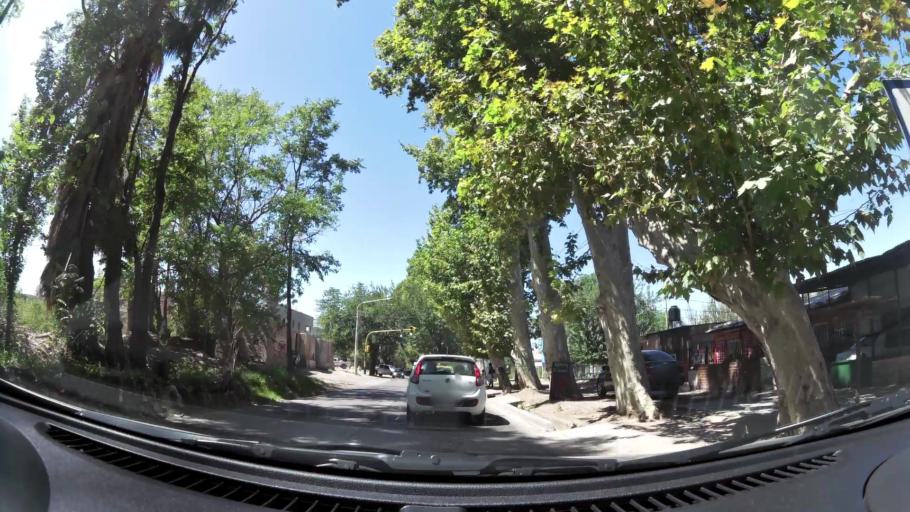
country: AR
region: Mendoza
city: Las Heras
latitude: -32.8697
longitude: -68.8032
